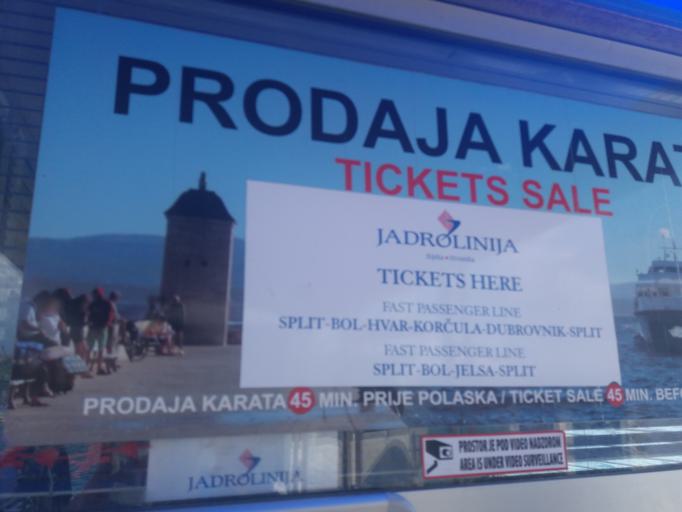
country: HR
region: Splitsko-Dalmatinska
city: Bol
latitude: 43.2617
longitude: 16.6579
